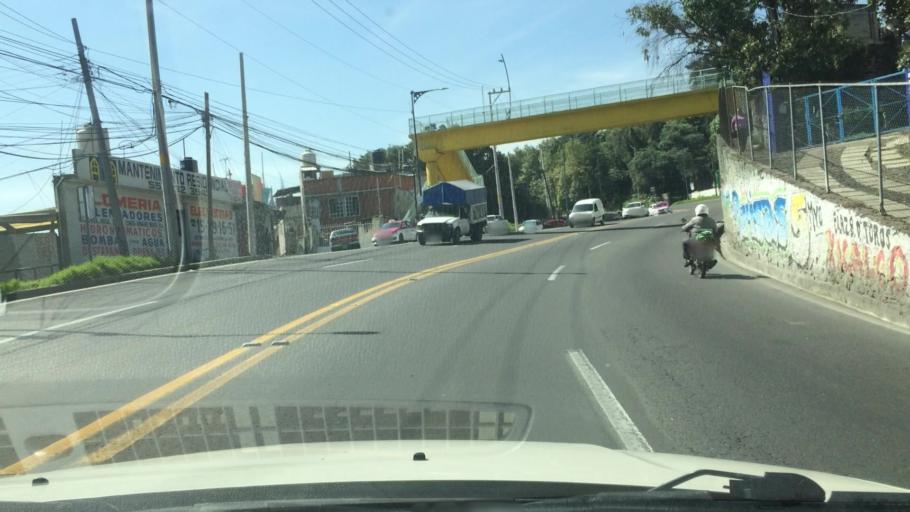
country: MX
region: Mexico City
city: Tlalpan
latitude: 19.2488
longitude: -99.1726
